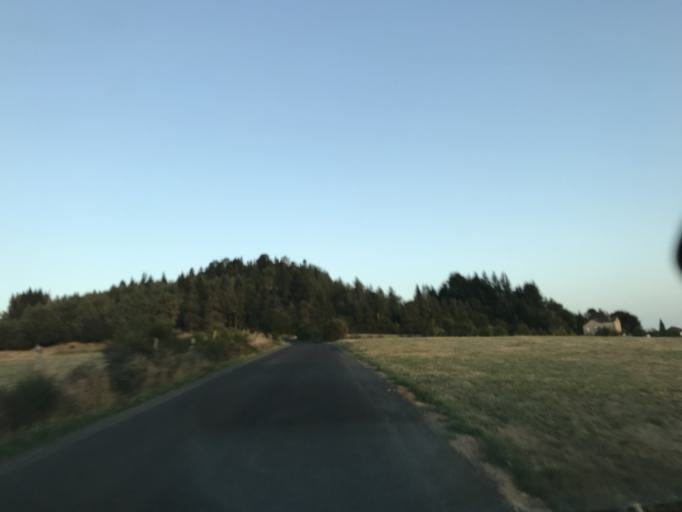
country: FR
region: Rhone-Alpes
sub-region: Departement de l'Ardeche
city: Saint-Agreve
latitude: 45.0146
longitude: 4.3899
